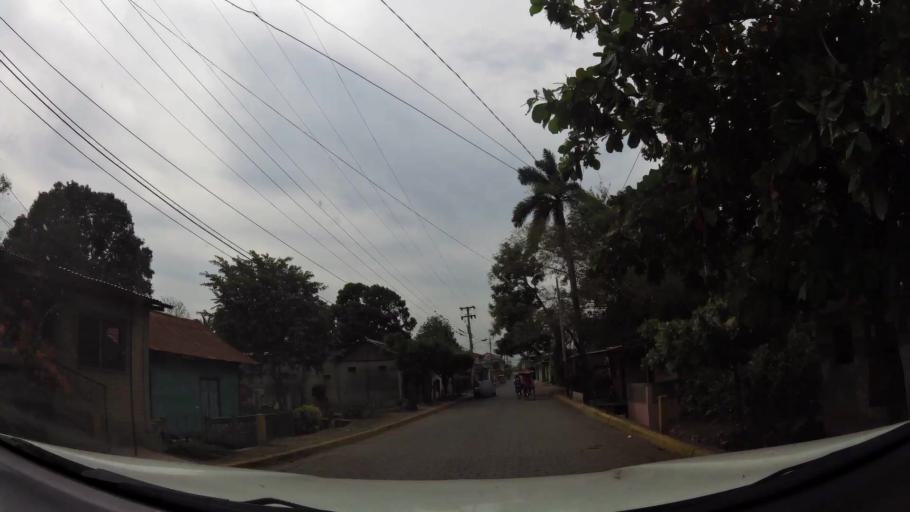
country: NI
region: Rivas
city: Rivas
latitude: 11.4355
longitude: -85.8293
